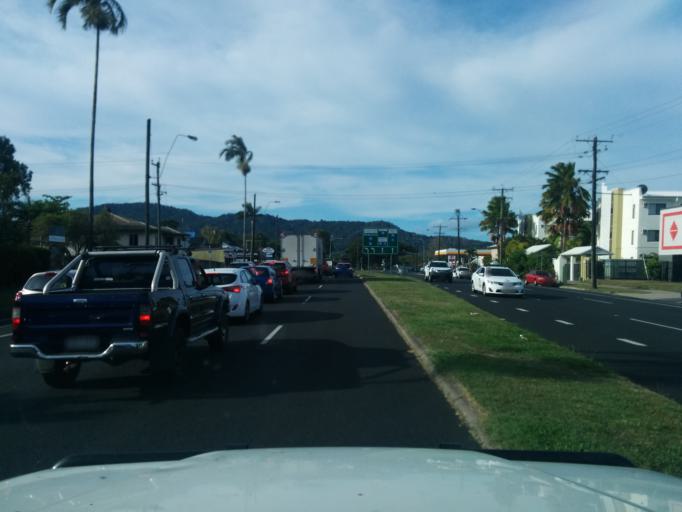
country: AU
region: Queensland
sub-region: Cairns
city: Cairns
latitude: -16.9204
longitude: 145.7403
